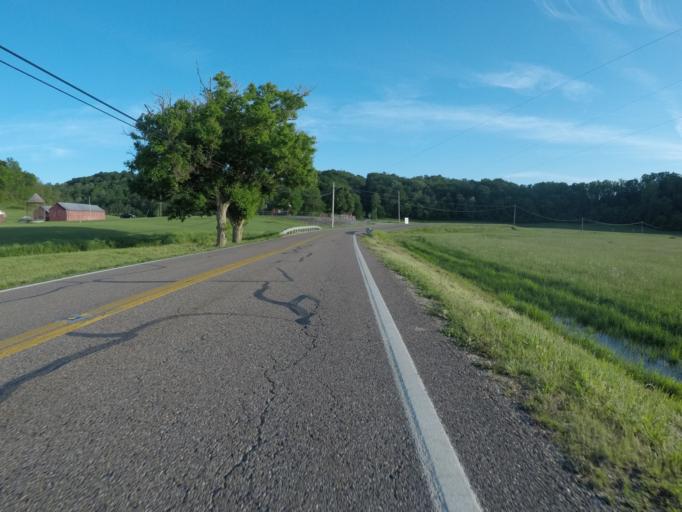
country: US
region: West Virginia
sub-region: Cabell County
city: Huntington
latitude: 38.5245
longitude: -82.4598
